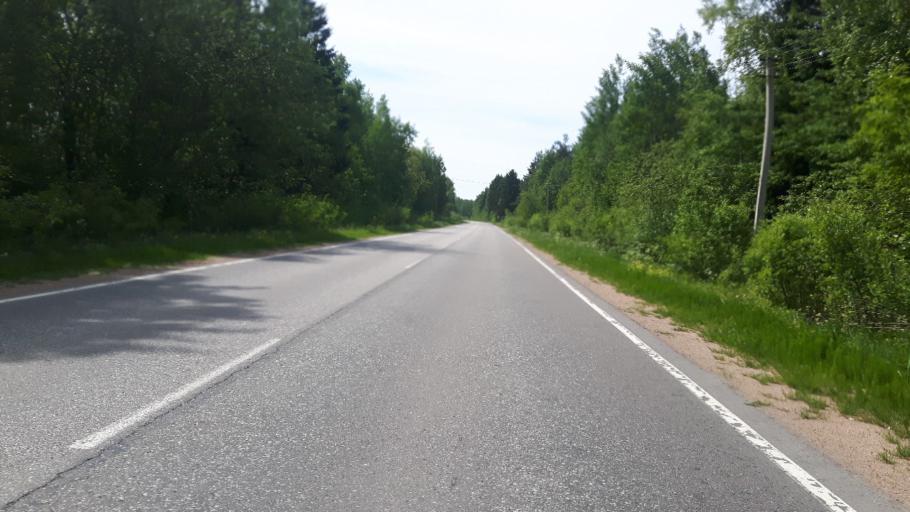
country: RU
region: Leningrad
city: Ust'-Luga
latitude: 59.6495
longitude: 28.2326
